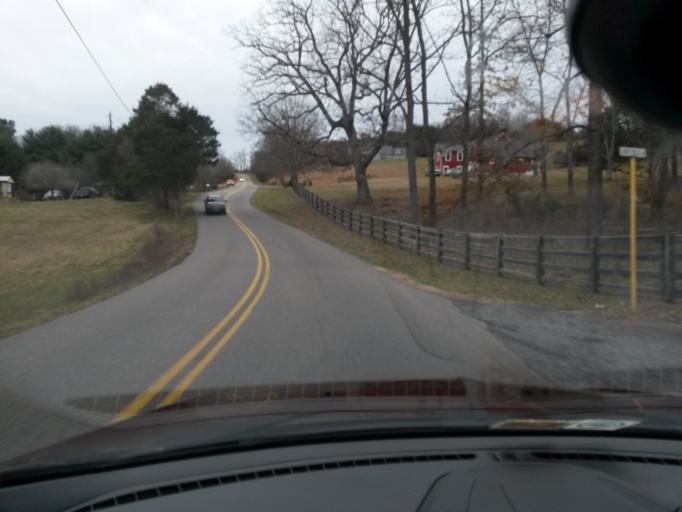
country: US
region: Virginia
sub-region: Rockbridge County
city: East Lexington
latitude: 37.7887
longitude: -79.3730
